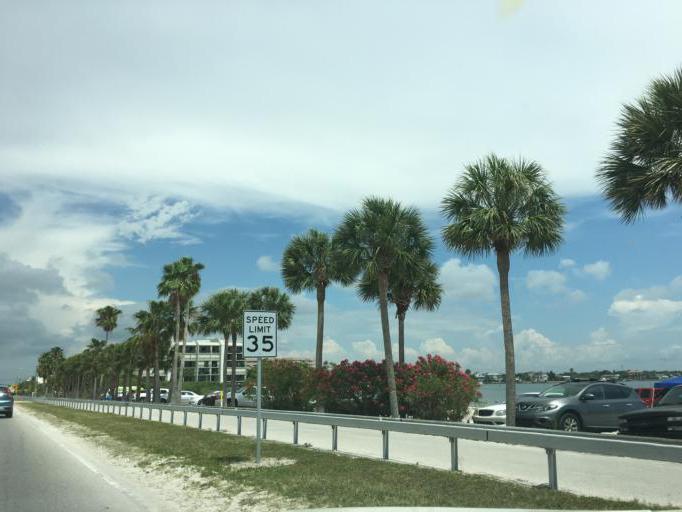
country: US
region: Florida
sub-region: Pinellas County
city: Dunedin
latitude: 28.0511
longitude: -82.7919
